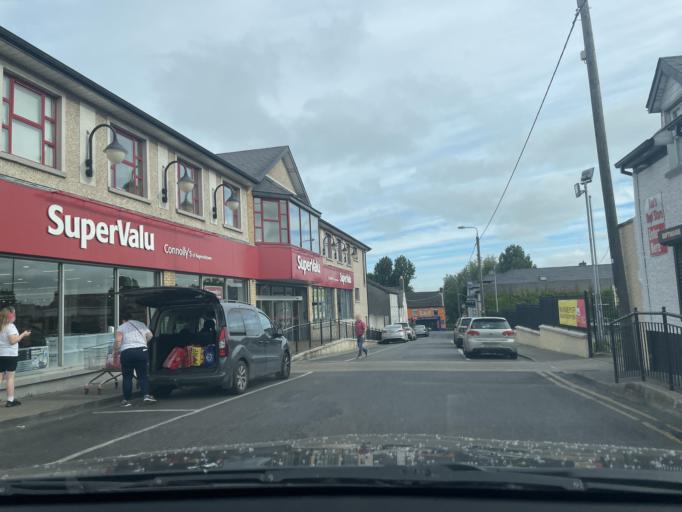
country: IE
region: Leinster
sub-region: County Carlow
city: Bagenalstown
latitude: 52.7020
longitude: -6.9605
